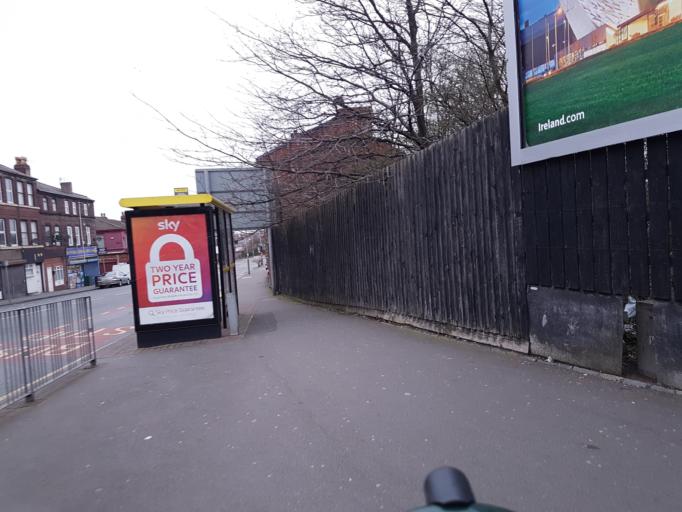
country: GB
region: England
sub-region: Sefton
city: Litherland
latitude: 53.4483
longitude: -2.9666
